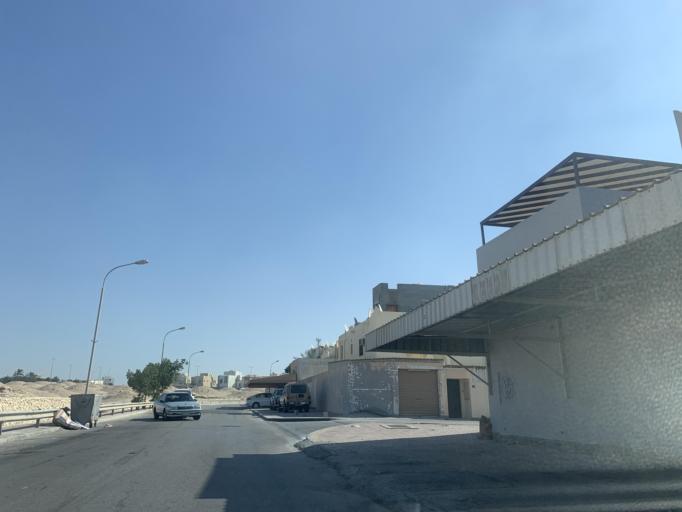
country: BH
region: Central Governorate
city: Madinat Hamad
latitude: 26.1173
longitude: 50.4986
